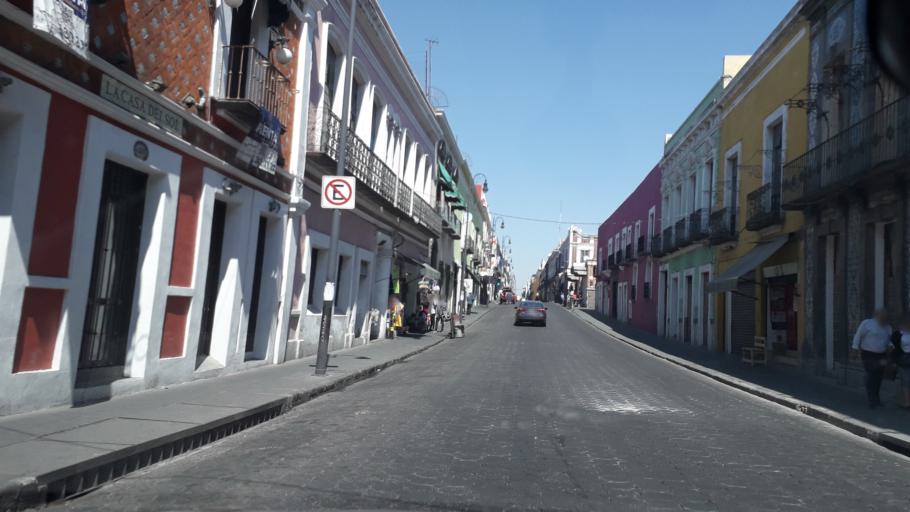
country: MX
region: Puebla
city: Puebla
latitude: 19.0424
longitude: -98.1928
